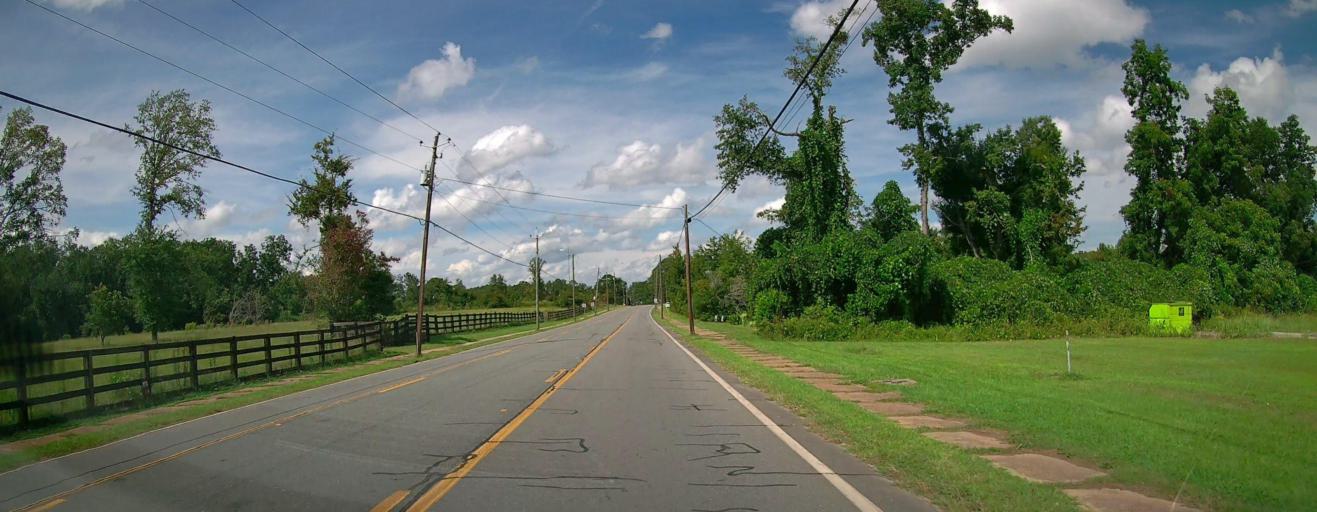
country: US
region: Georgia
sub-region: Talbot County
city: Talbotton
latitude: 32.6835
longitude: -84.5400
